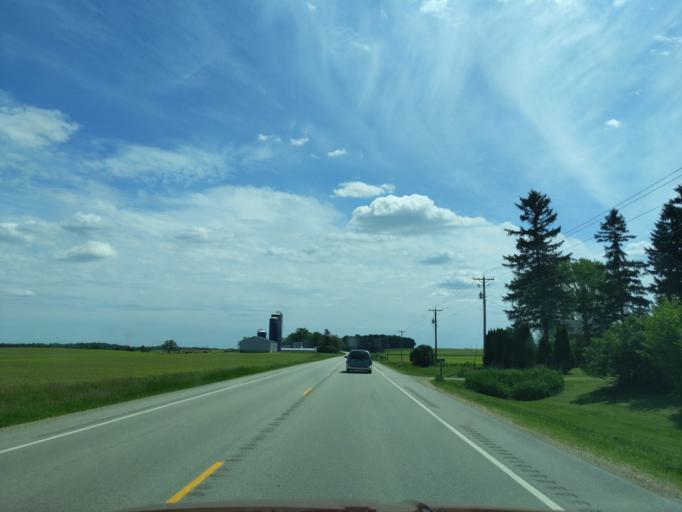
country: US
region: Wisconsin
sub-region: Columbia County
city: Poynette
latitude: 43.3590
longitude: -89.3285
